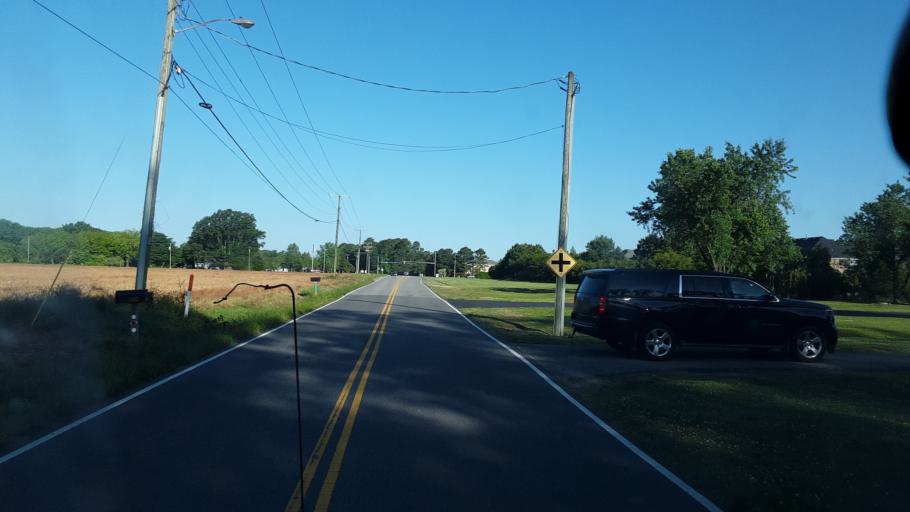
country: US
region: Virginia
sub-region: City of Virginia Beach
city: Virginia Beach
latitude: 36.7211
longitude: -76.0480
